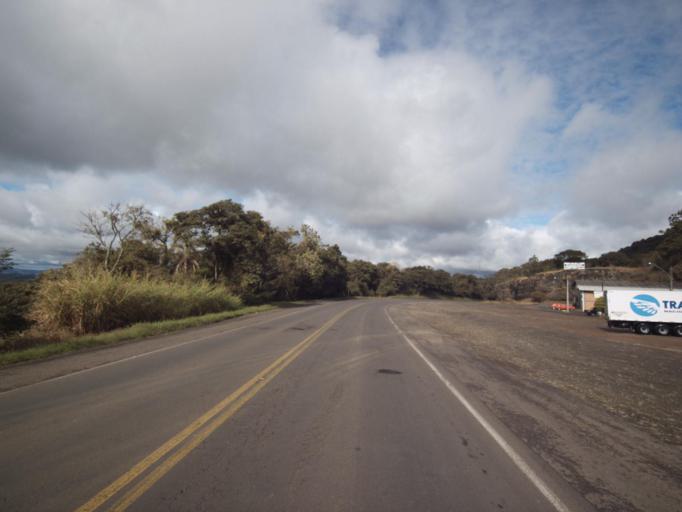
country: BR
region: Santa Catarina
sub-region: Concordia
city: Concordia
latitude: -27.2047
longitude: -51.9492
